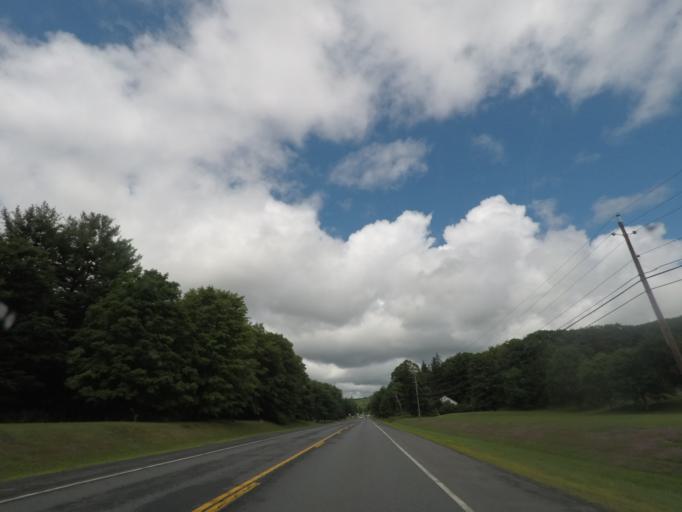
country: US
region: Massachusetts
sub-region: Berkshire County
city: Williamstown
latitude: 42.6386
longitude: -73.3593
